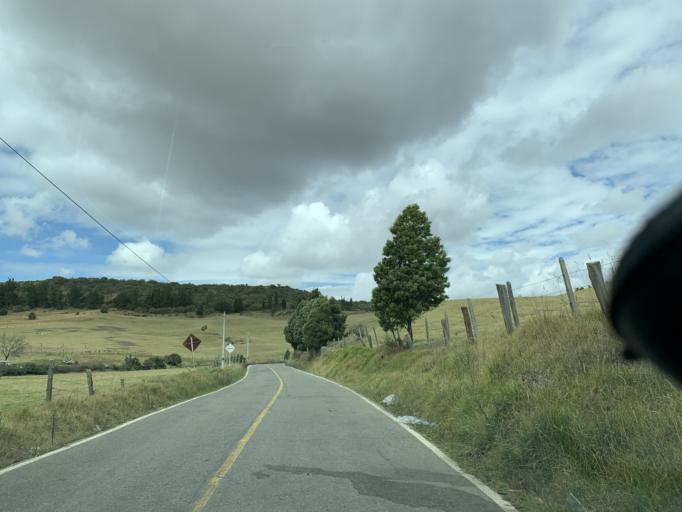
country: CO
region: Boyaca
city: Toca
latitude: 5.5710
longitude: -73.2257
